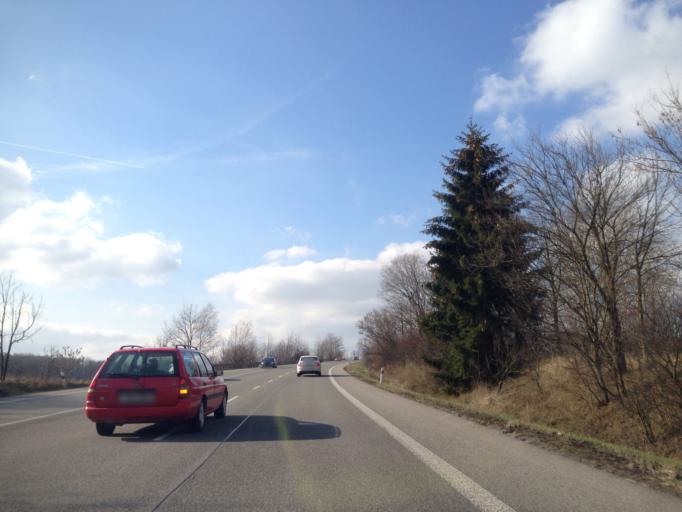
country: CZ
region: Kralovehradecky
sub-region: Okres Jicin
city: Sobotka
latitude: 50.4558
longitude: 15.2236
